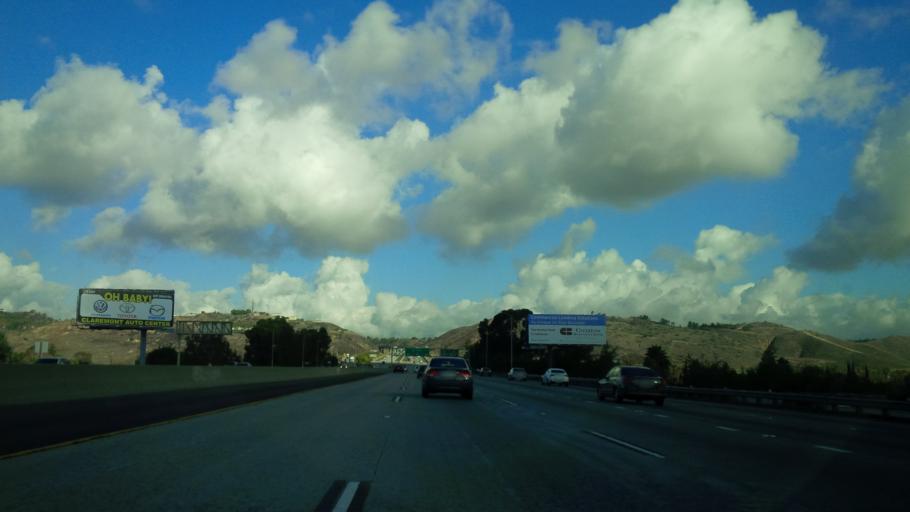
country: US
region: California
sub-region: Los Angeles County
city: Diamond Bar
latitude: 34.0552
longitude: -117.8033
